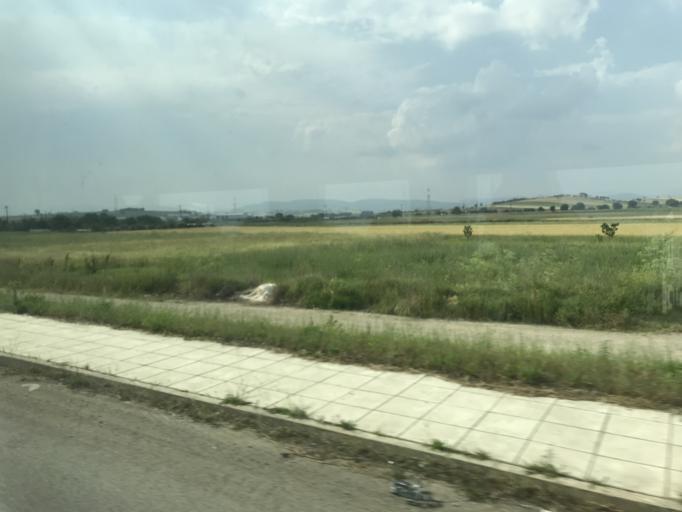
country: GR
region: East Macedonia and Thrace
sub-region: Nomos Evrou
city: Alexandroupoli
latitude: 40.8558
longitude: 25.9307
